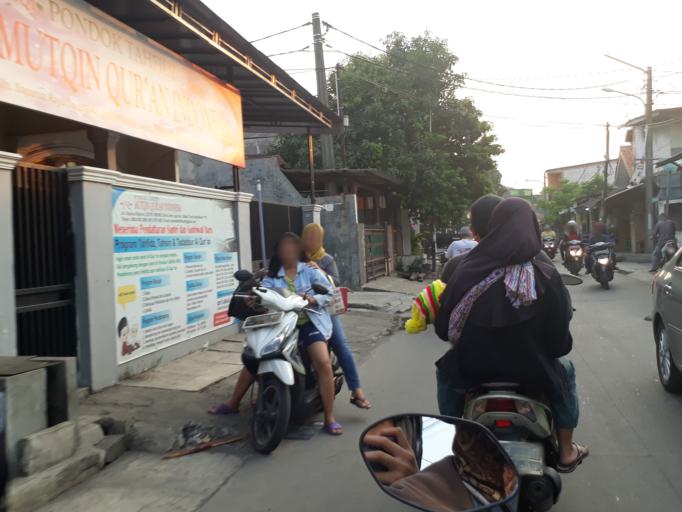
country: ID
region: West Java
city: Bekasi
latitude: -6.2423
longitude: 107.0408
